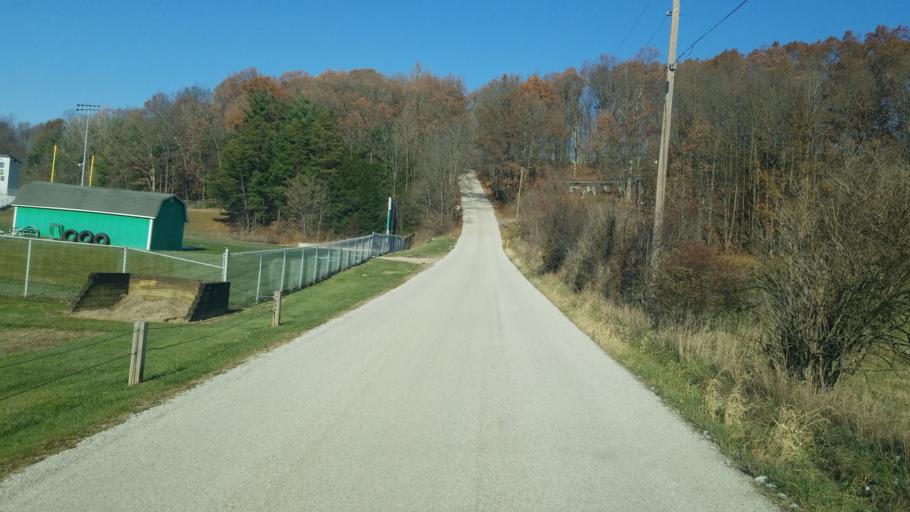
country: US
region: Ohio
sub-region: Sandusky County
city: Bellville
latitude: 40.6104
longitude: -82.4713
